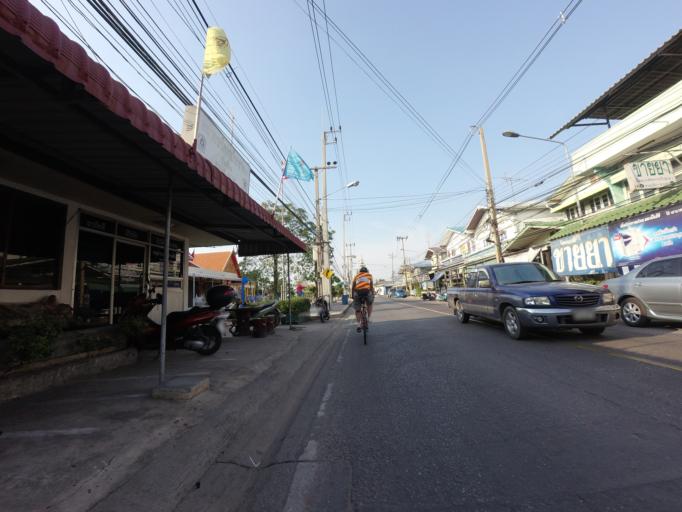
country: TH
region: Samut Sakhon
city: Samut Sakhon
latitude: 13.5428
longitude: 100.2788
